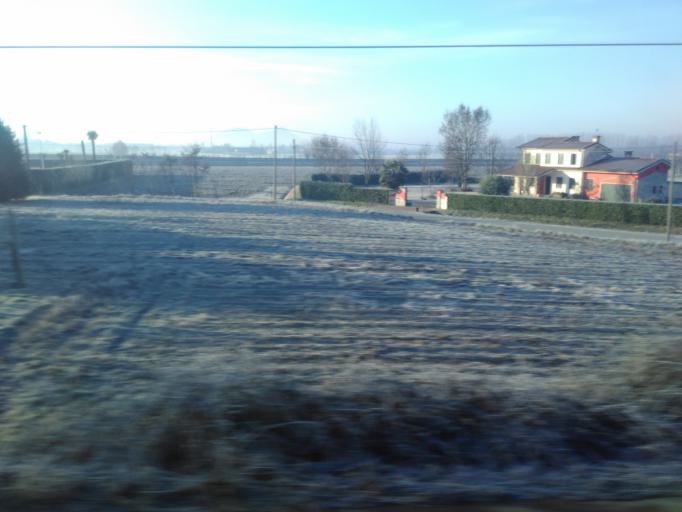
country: IT
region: Veneto
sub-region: Provincia di Padova
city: Campodoro
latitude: 45.4695
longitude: 11.7469
